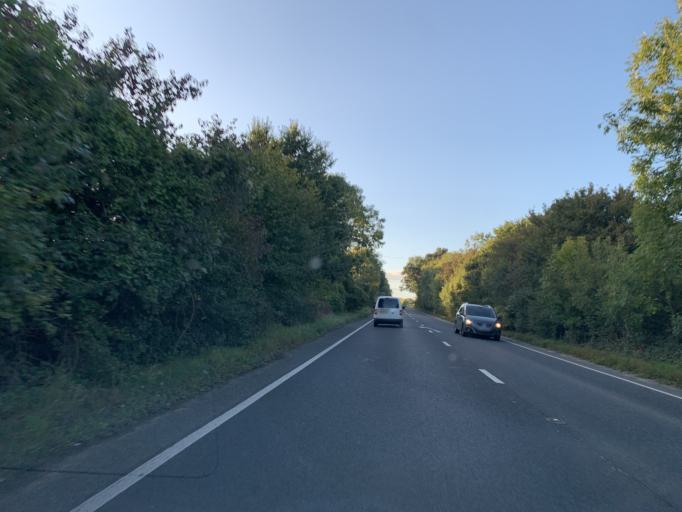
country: GB
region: England
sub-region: Wiltshire
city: Whiteparish
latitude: 51.0088
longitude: -1.6750
